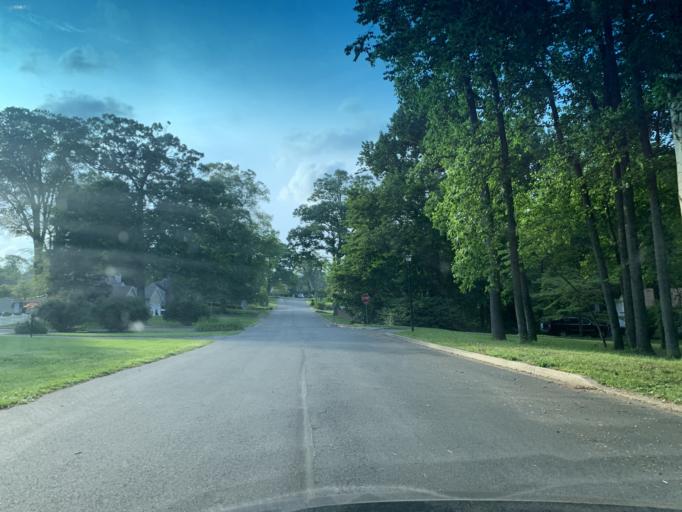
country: US
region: Maryland
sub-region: Harford County
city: North Bel Air
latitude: 39.5436
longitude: -76.3565
